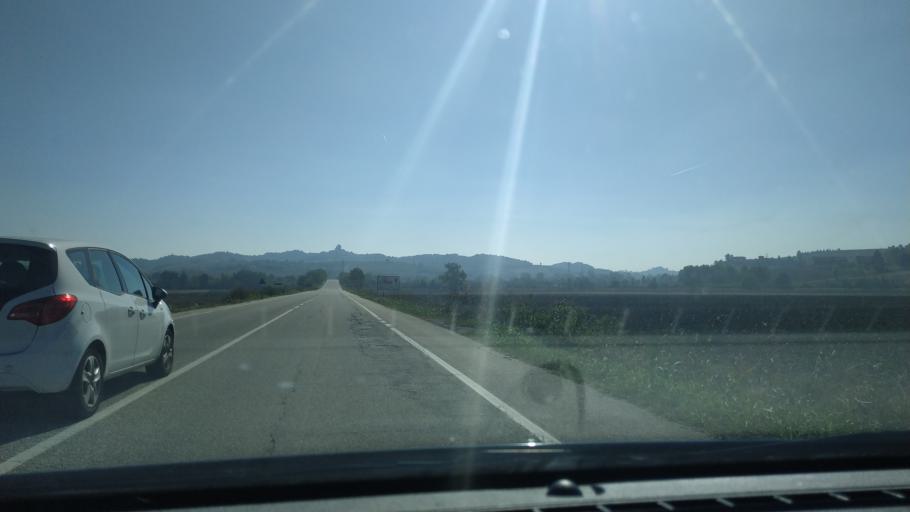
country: IT
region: Piedmont
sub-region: Provincia di Alessandria
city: Cereseto
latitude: 45.1116
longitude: 8.3271
